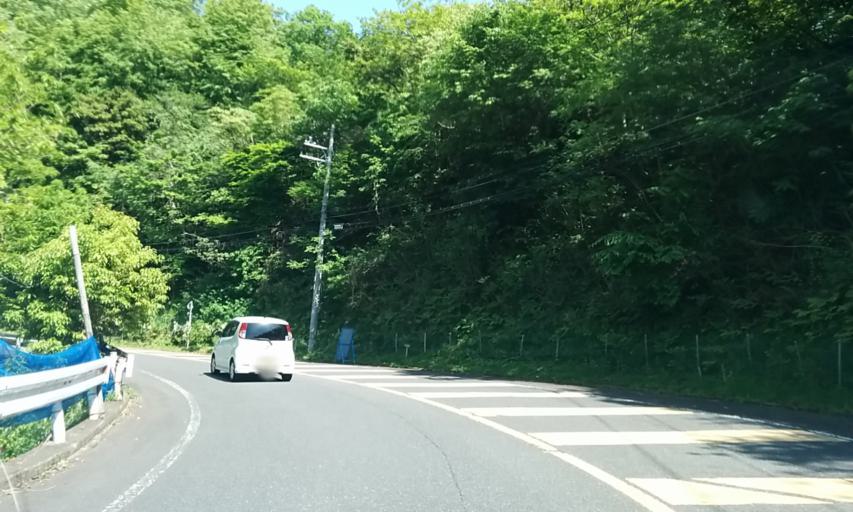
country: JP
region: Kyoto
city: Maizuru
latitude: 35.4609
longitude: 135.3525
